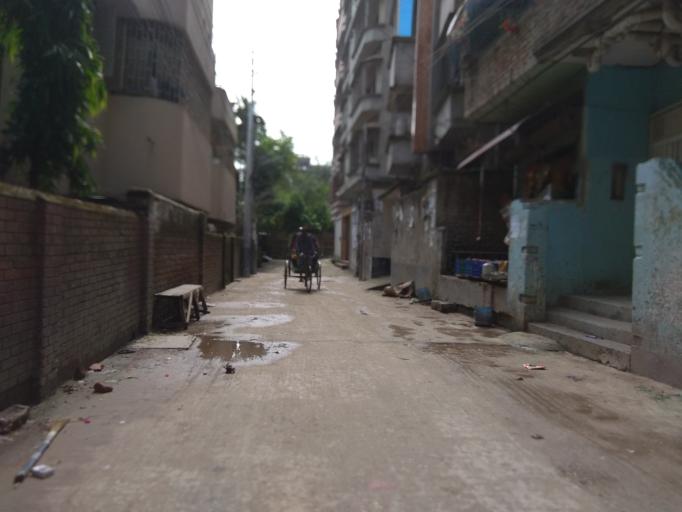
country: BD
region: Dhaka
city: Azimpur
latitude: 23.7979
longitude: 90.3586
